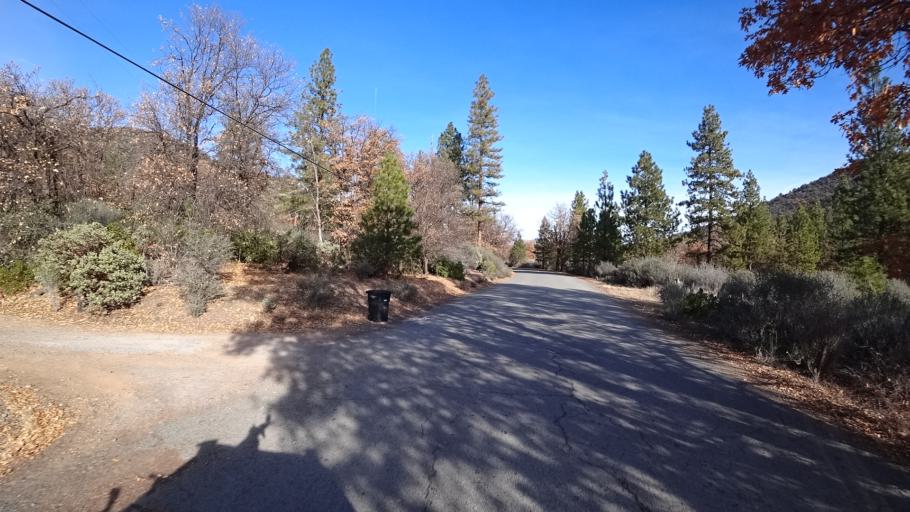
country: US
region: California
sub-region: Siskiyou County
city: Montague
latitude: 41.6104
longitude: -122.5775
